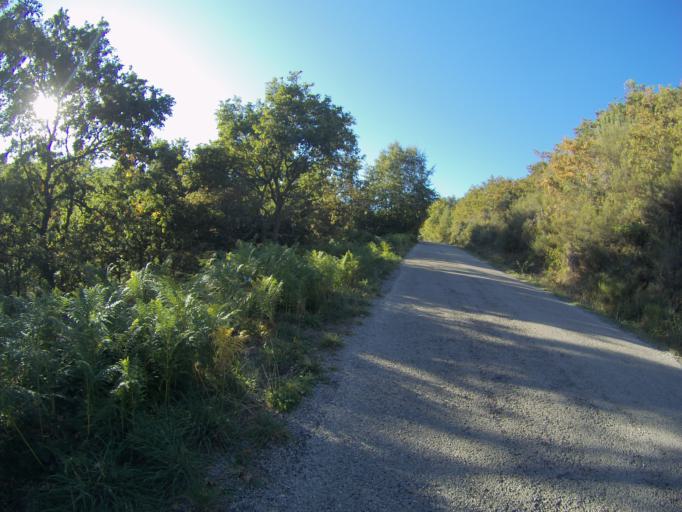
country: ES
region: Castille and Leon
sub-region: Provincia de Leon
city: Vega de Valcarce
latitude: 42.7008
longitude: -7.0158
